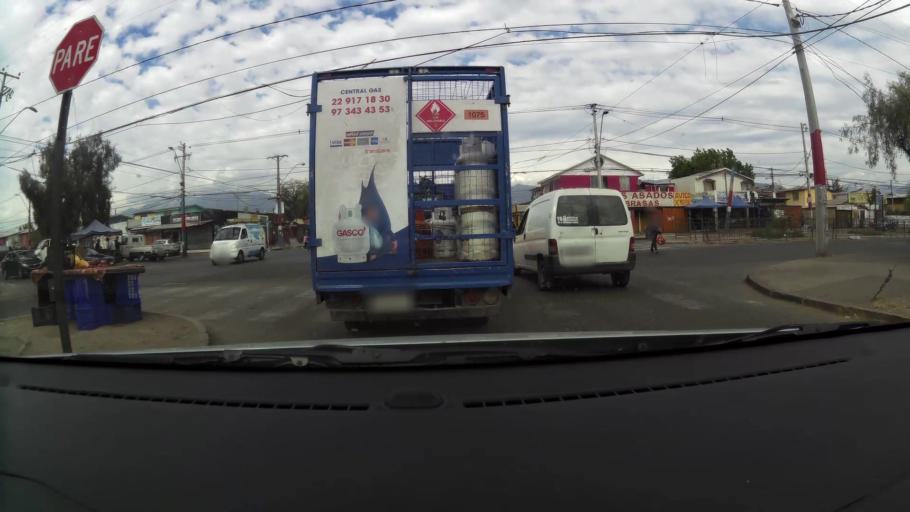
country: CL
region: Santiago Metropolitan
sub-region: Provincia de Cordillera
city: Puente Alto
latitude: -33.6213
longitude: -70.6129
